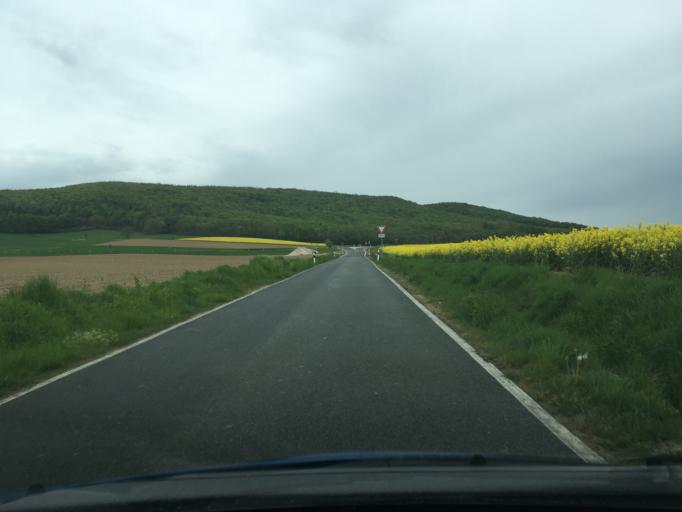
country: DE
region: Lower Saxony
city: Luerdissen
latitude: 51.9512
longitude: 9.6367
